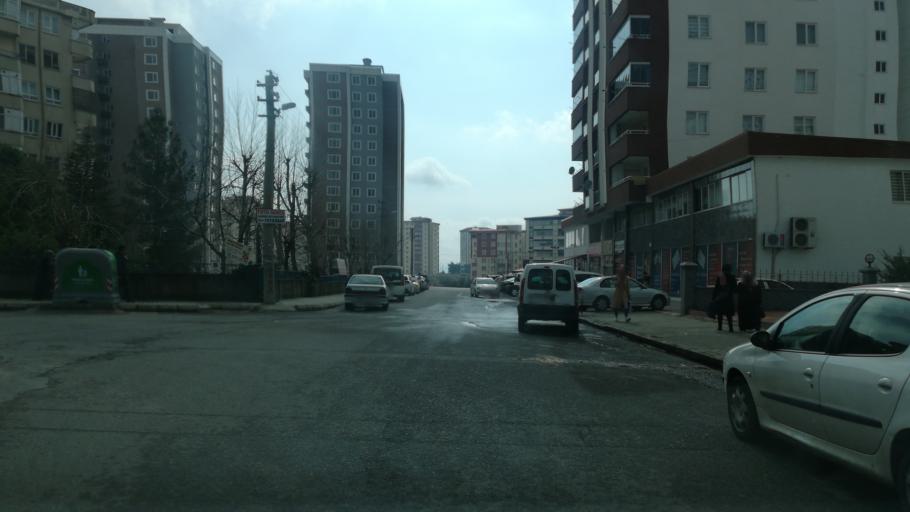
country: TR
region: Kahramanmaras
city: Kahramanmaras
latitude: 37.5831
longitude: 36.8961
